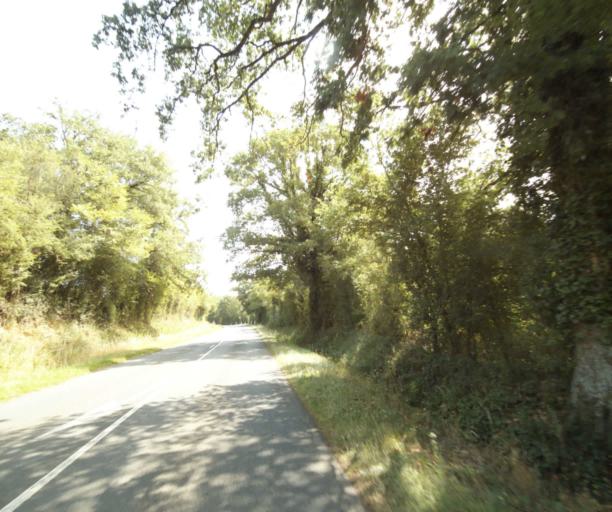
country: FR
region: Pays de la Loire
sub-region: Departement de la Sarthe
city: Sable-sur-Sarthe
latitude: 47.8284
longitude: -0.3829
